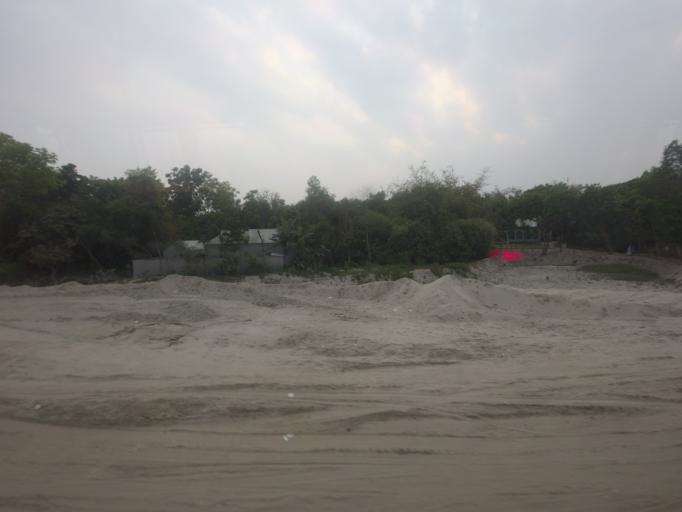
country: BD
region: Dhaka
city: Tangail
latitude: 24.2083
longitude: 89.9810
